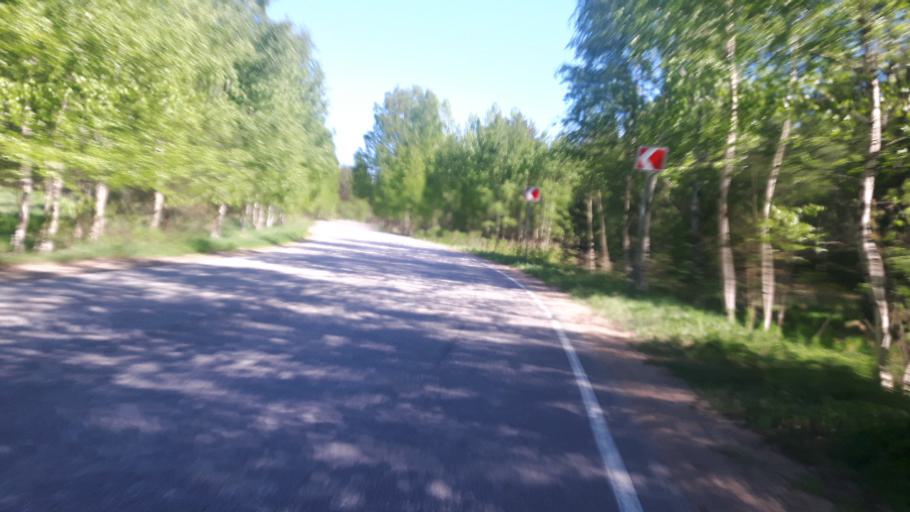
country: RU
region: Leningrad
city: Glebychevo
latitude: 60.2807
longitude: 28.8842
